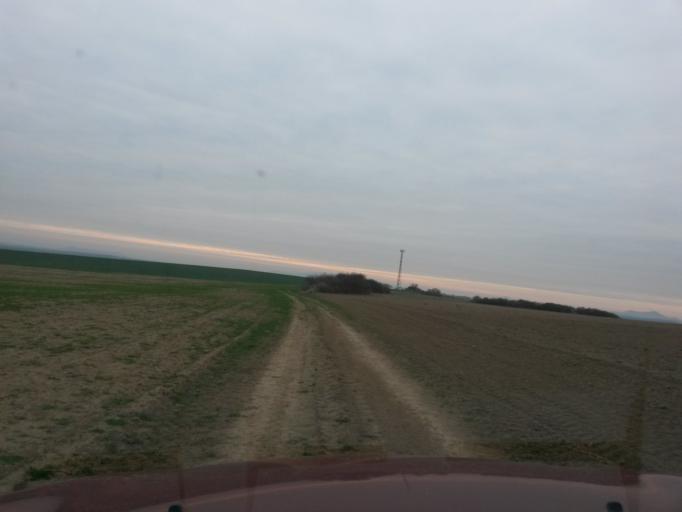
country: SK
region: Kosicky
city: Secovce
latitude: 48.6443
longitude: 21.6258
